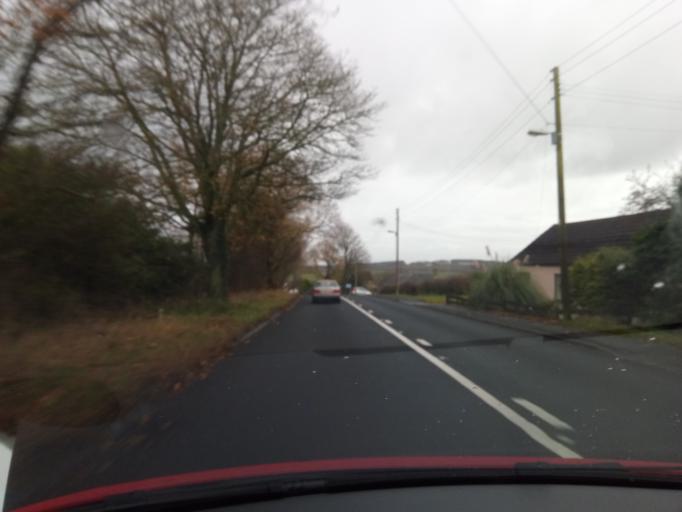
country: GB
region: England
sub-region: County Durham
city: High Etherley
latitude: 54.6408
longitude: -1.7442
